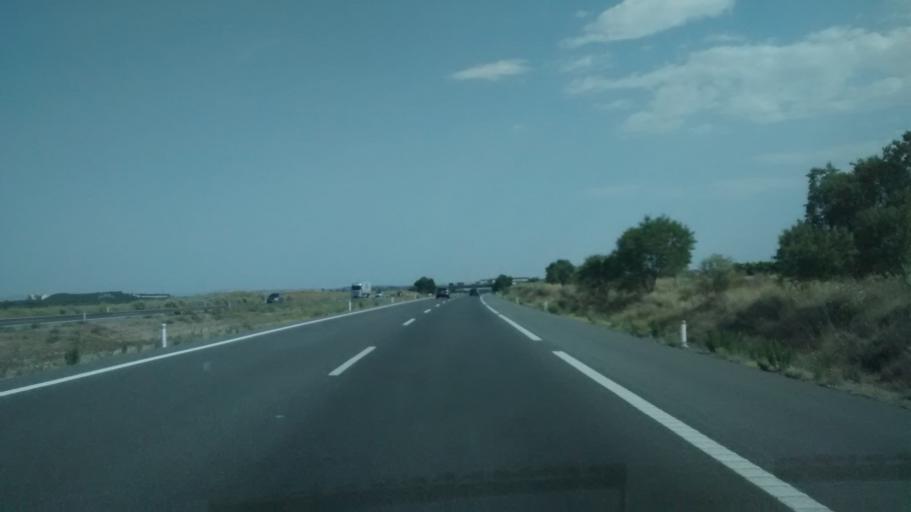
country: ES
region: Navarre
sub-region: Provincia de Navarra
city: Murchante
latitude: 42.0479
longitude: -1.6679
